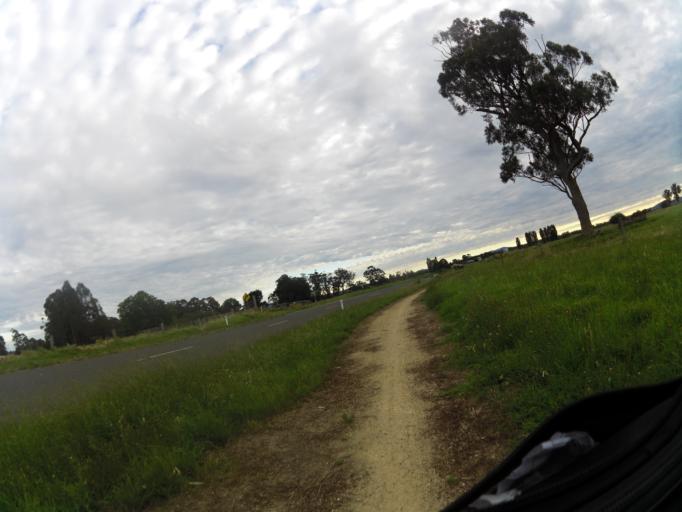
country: AU
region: Victoria
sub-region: East Gippsland
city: Lakes Entrance
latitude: -37.7246
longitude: 148.4409
